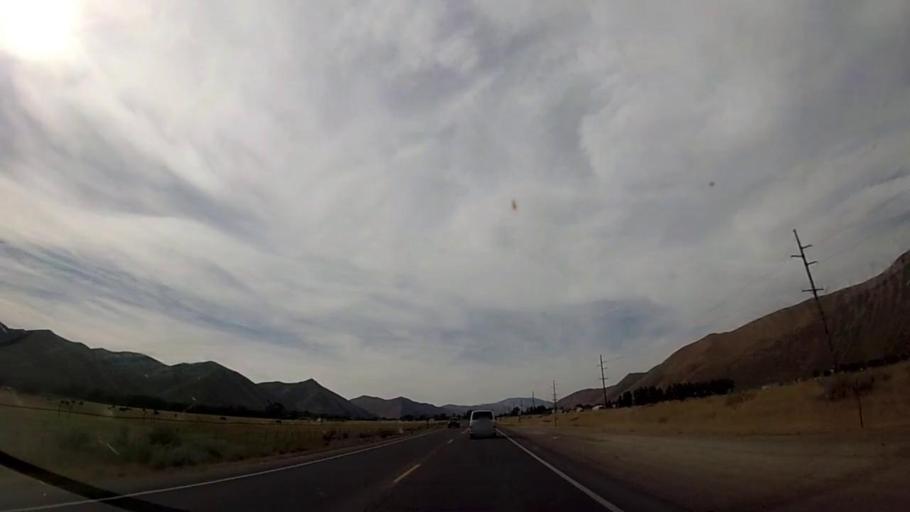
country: US
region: Idaho
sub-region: Blaine County
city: Bellevue
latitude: 43.4808
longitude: -114.2715
